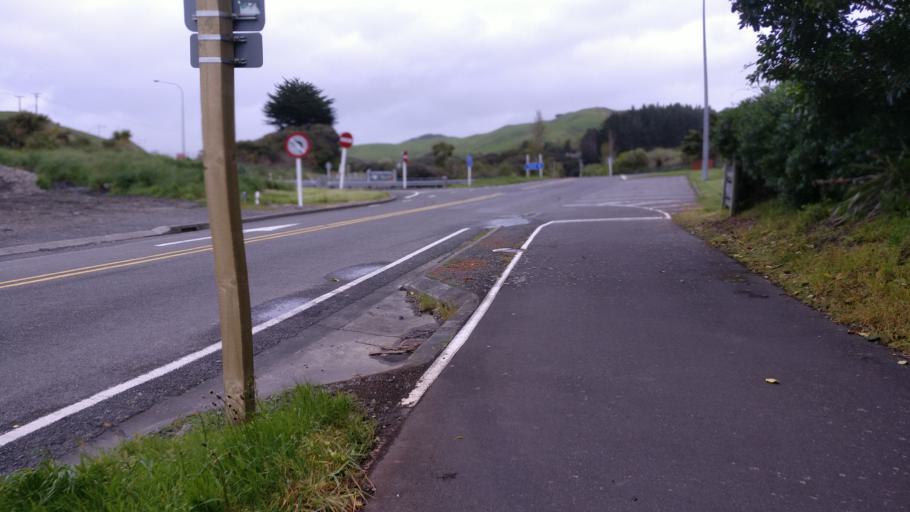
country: NZ
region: Wellington
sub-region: Porirua City
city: Porirua
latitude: -41.0553
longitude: 174.8762
